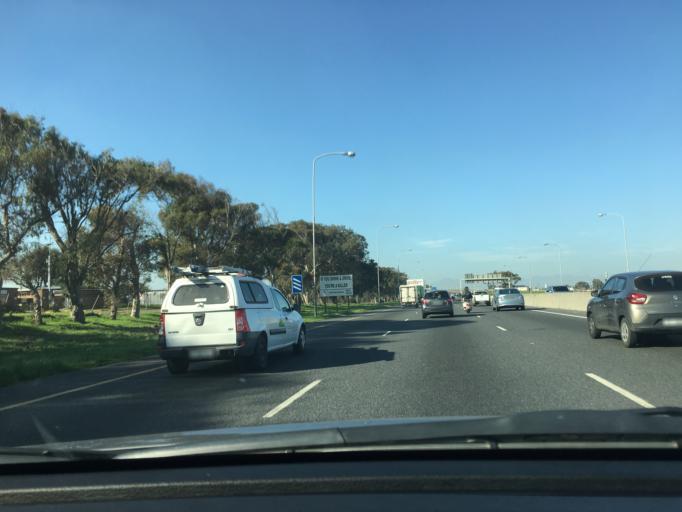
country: ZA
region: Western Cape
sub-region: City of Cape Town
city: Rondebosch
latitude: -33.9500
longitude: 18.5148
